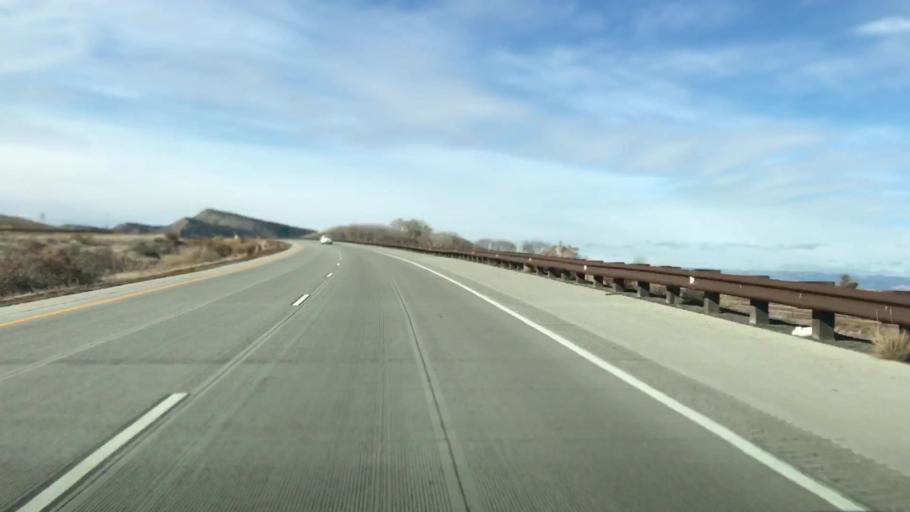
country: US
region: Colorado
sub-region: Mesa County
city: Loma
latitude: 39.1774
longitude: -108.8041
